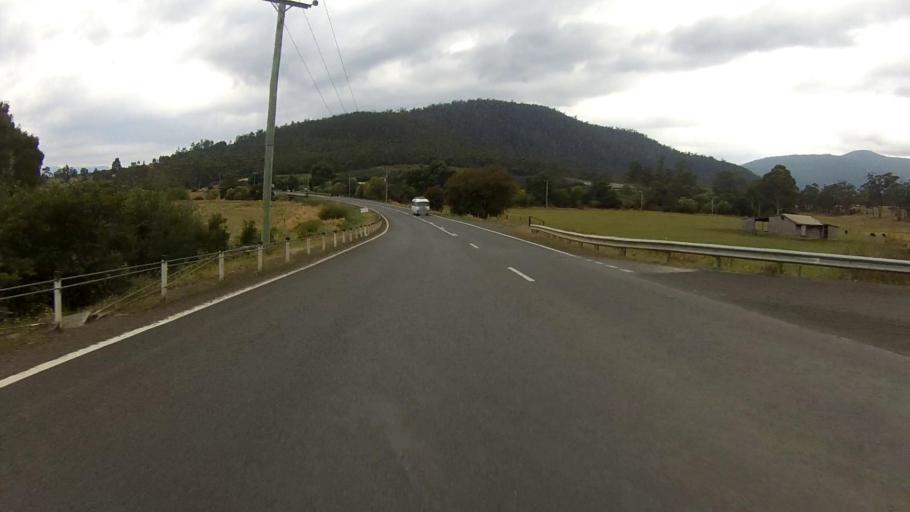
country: AU
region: Tasmania
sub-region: Huon Valley
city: Franklin
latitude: -43.0716
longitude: 147.0389
